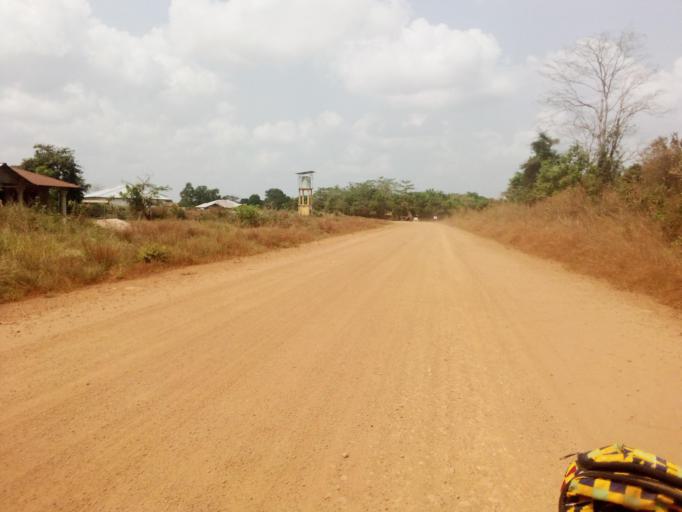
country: SL
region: Southern Province
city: Mogbwemo
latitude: 7.6642
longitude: -12.2732
